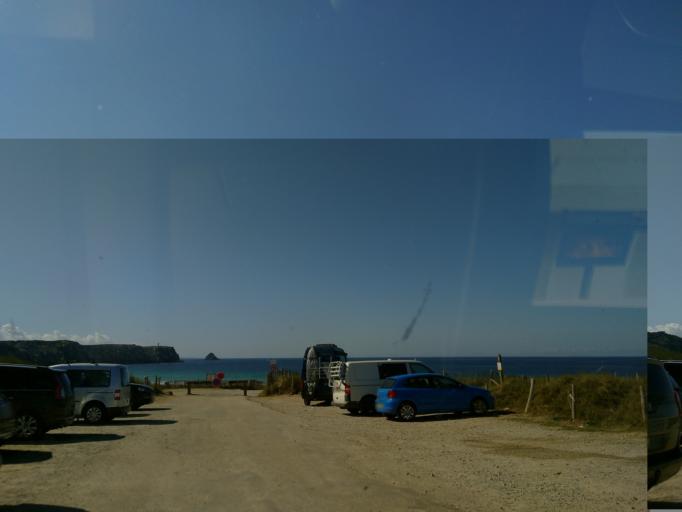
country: FR
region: Brittany
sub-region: Departement du Finistere
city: Camaret-sur-Mer
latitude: 48.2773
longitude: -4.6168
